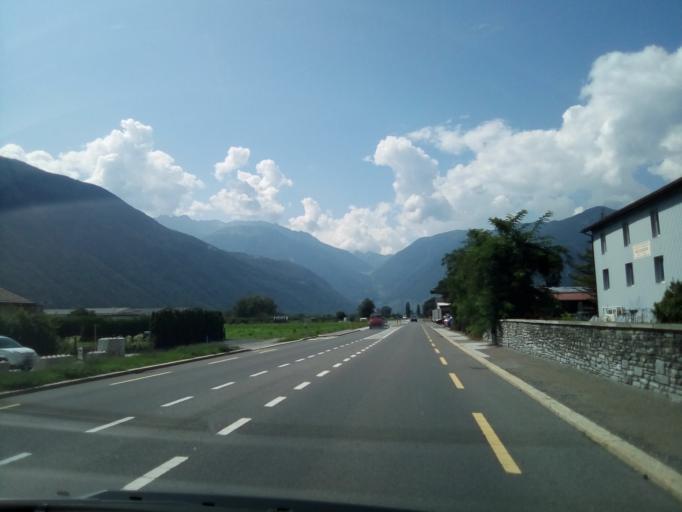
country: CH
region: Valais
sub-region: Martigny District
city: Charrat-les-Chenes
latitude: 46.1249
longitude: 7.1236
